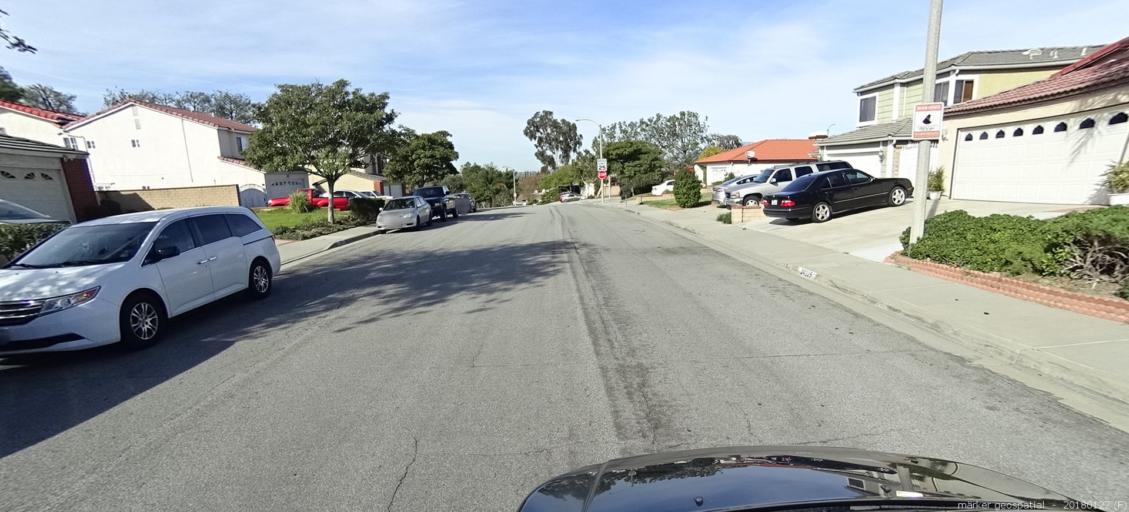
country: US
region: California
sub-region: Los Angeles County
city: Diamond Bar
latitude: 34.0345
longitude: -117.7930
